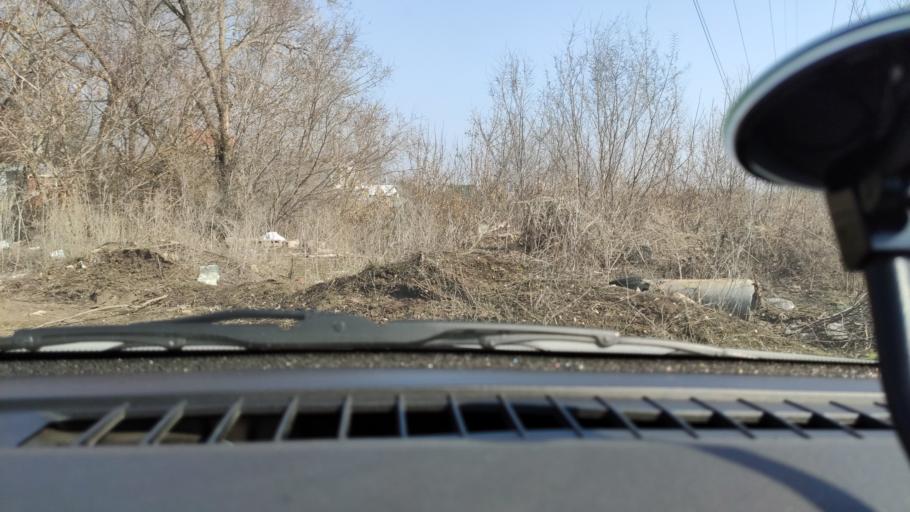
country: RU
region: Samara
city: Samara
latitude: 53.1802
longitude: 50.2368
